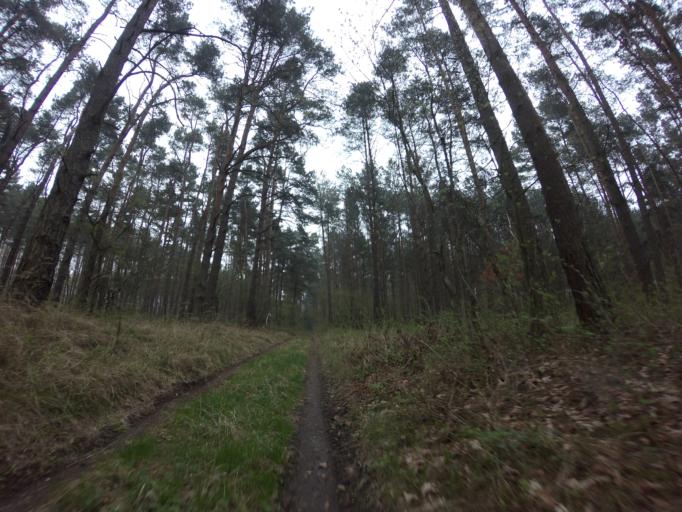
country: PL
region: West Pomeranian Voivodeship
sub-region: Powiat choszczenski
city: Recz
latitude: 53.1832
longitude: 15.5231
